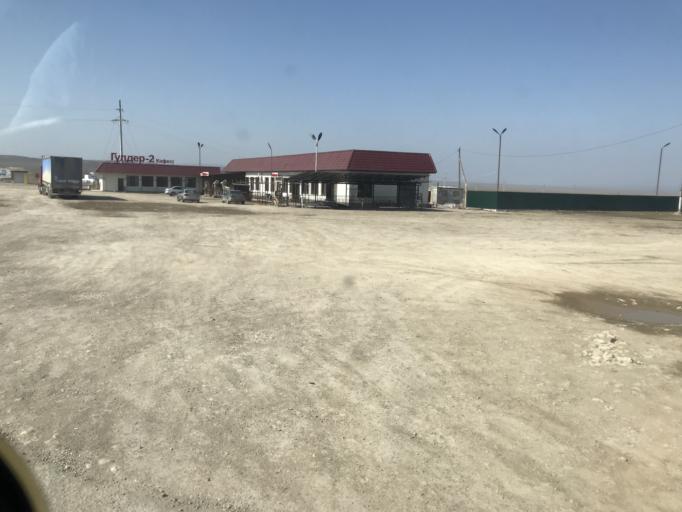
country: KZ
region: Zhambyl
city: Georgiyevka
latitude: 43.4124
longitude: 75.0630
